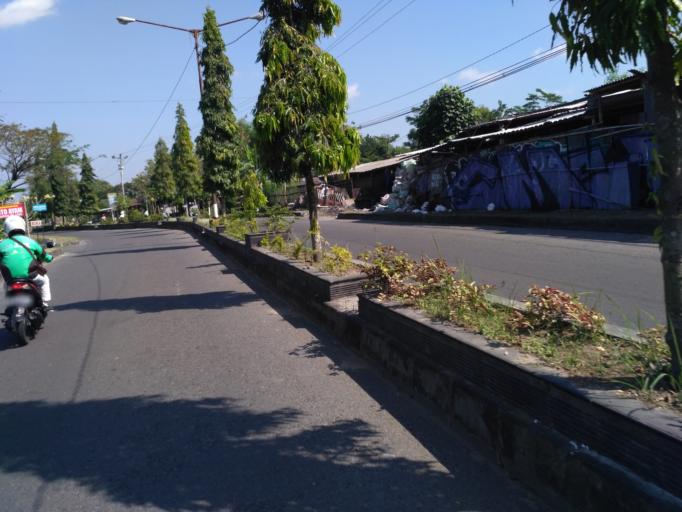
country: ID
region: Daerah Istimewa Yogyakarta
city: Depok
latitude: -7.7512
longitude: 110.4304
